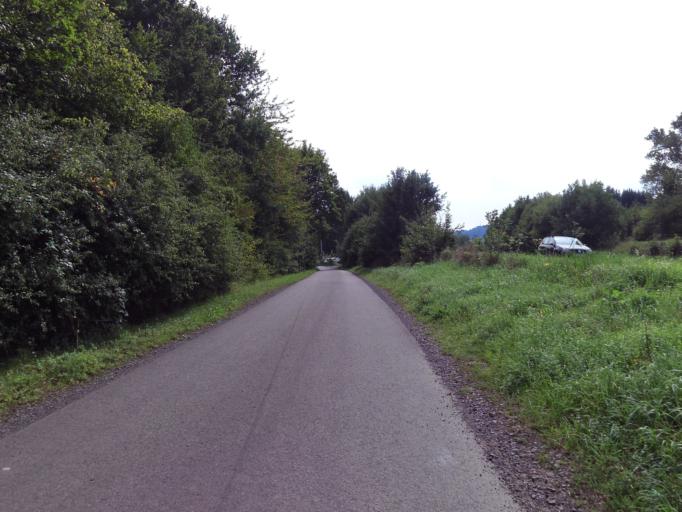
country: DE
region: Rheinland-Pfalz
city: Rockenhausen
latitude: 49.6375
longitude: 7.8220
